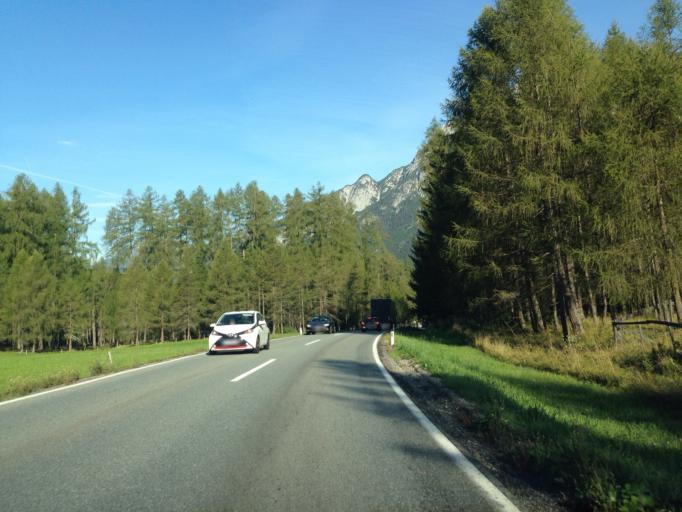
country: AT
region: Tyrol
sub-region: Politischer Bezirk Imst
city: Obsteig
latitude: 47.3060
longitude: 10.8906
